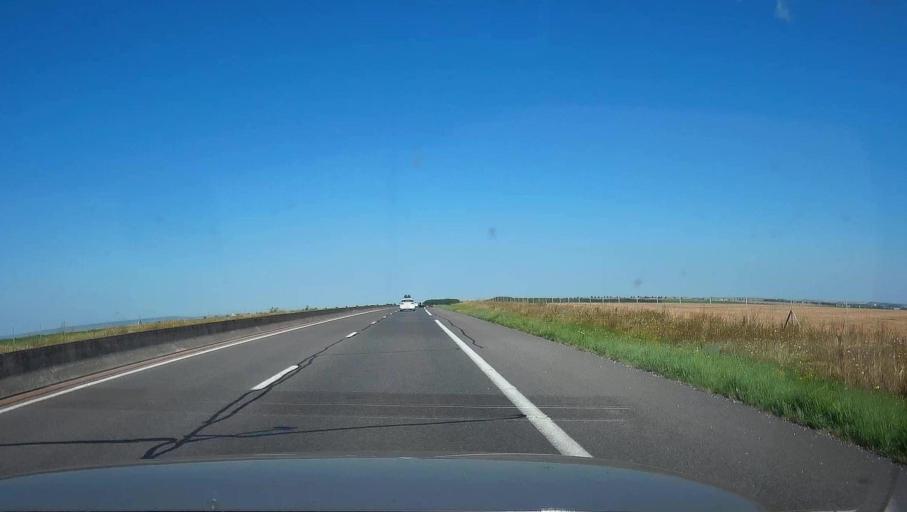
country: FR
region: Champagne-Ardenne
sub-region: Departement de la Marne
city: Fagnieres
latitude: 48.9251
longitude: 4.2834
